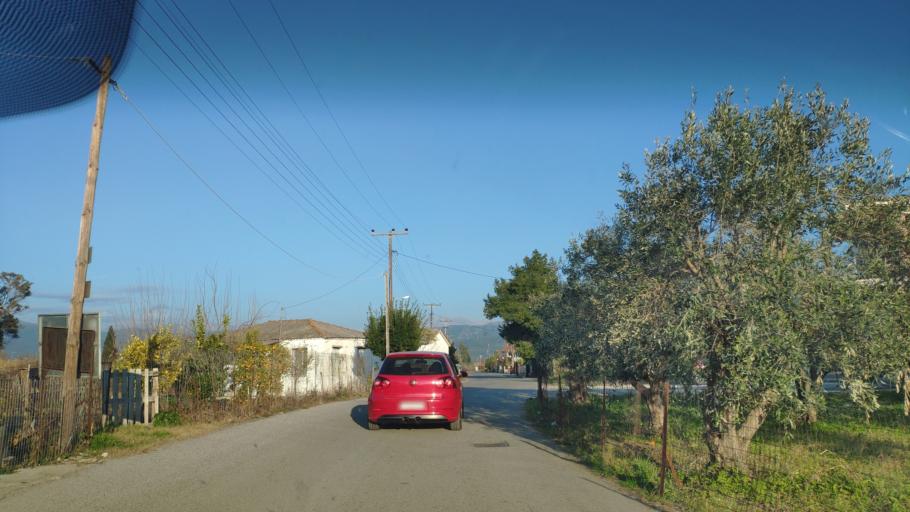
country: GR
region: West Greece
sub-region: Nomos Aitolias kai Akarnanias
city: Krikellos
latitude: 38.9281
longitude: 21.1432
